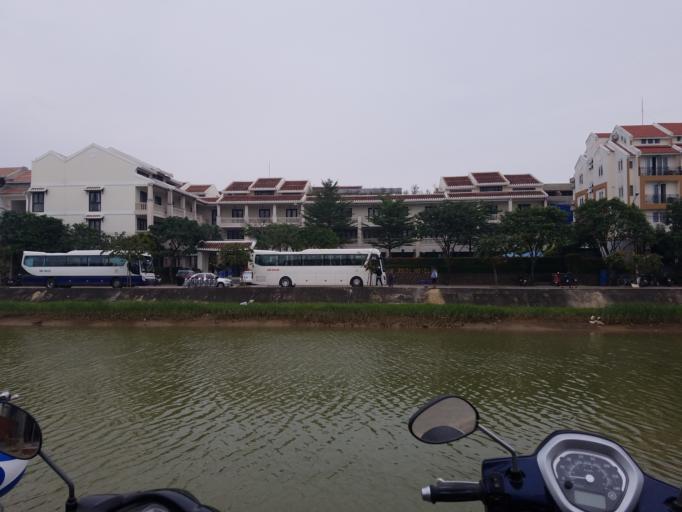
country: VN
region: Quang Nam
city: Hoi An
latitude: 15.8760
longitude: 108.3224
